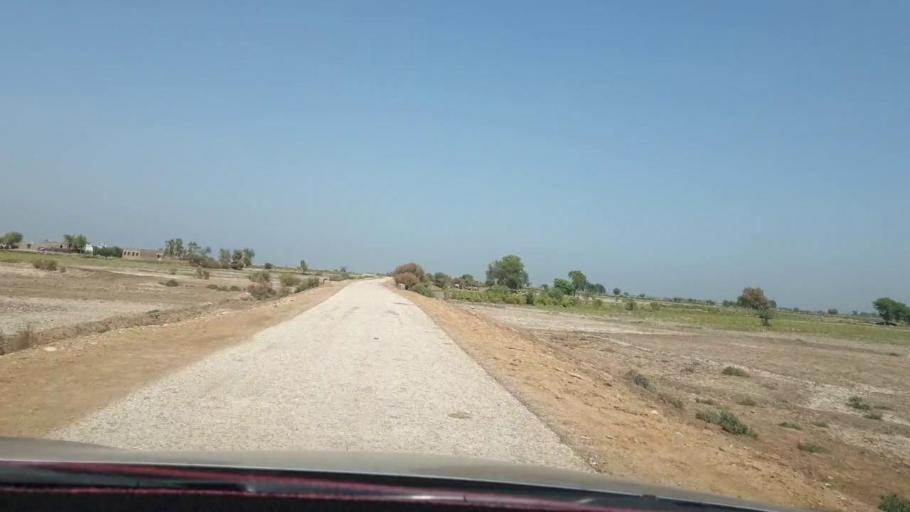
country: PK
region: Sindh
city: Warah
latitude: 27.5238
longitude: 67.7088
